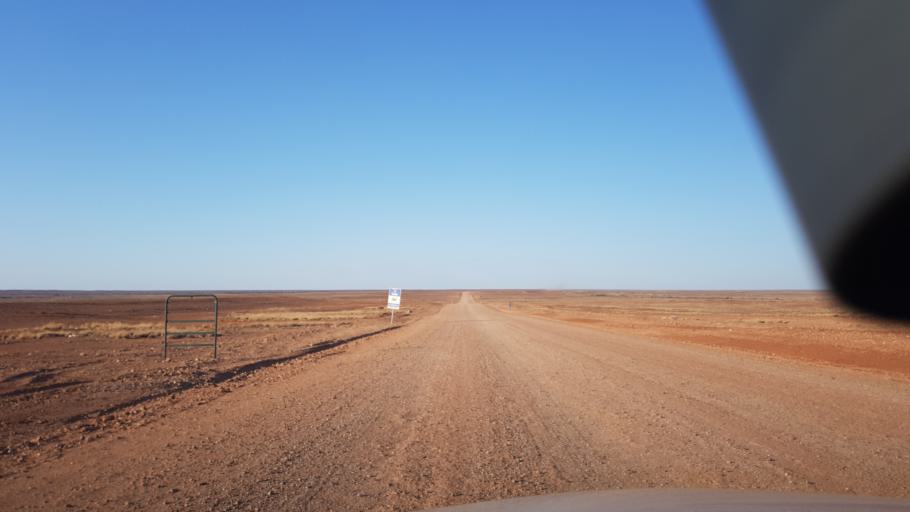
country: AU
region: South Australia
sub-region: Coober Pedy
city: Coober Pedy
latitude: -28.9757
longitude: 134.7712
